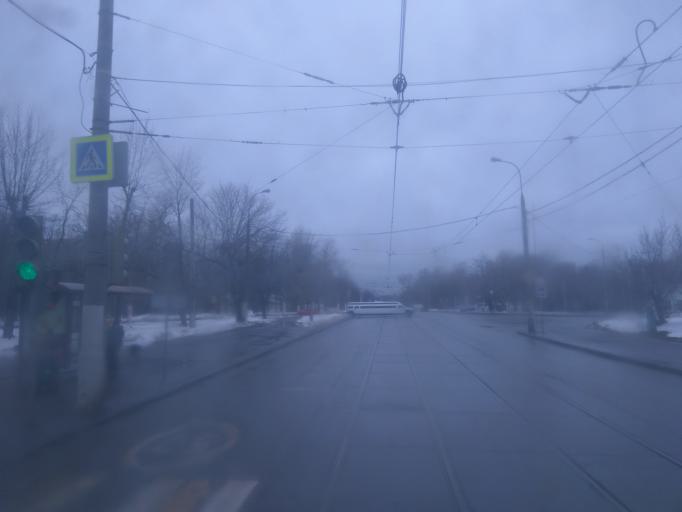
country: RU
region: Moskovskaya
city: Kozhukhovo
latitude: 55.6785
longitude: 37.6506
